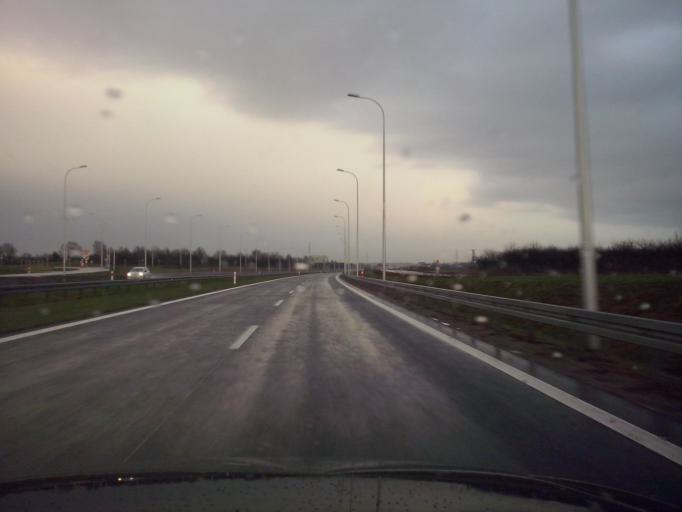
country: PL
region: Lublin Voivodeship
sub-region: Powiat lubelski
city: Jastkow
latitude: 51.2778
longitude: 22.4698
